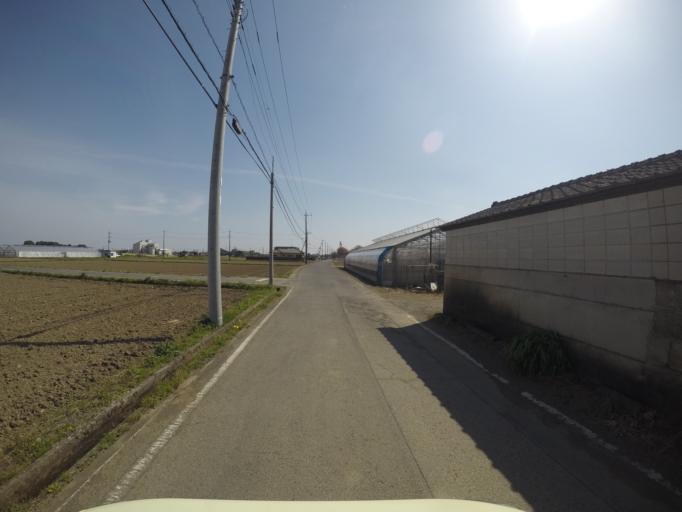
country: JP
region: Tochigi
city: Tochigi
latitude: 36.4431
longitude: 139.7232
